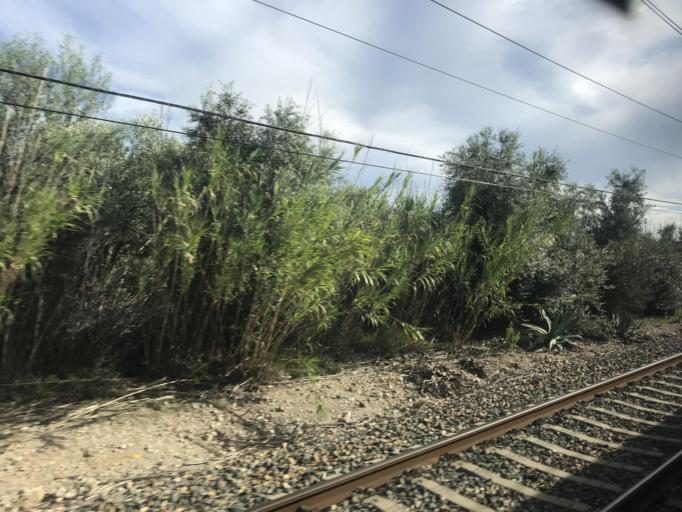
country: ES
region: Valencia
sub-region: Provincia de Castello
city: Vinaros
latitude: 40.4682
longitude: 0.4522
